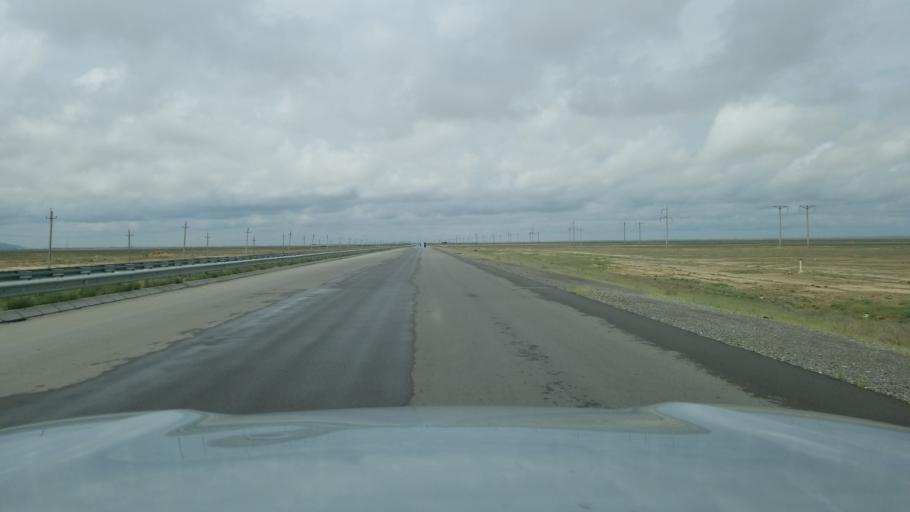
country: TM
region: Balkan
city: Gazanjyk
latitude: 39.2032
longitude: 55.7651
